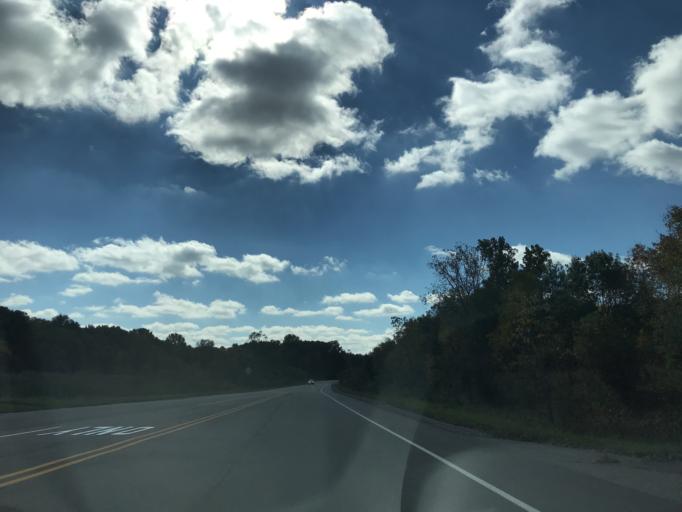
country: US
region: Michigan
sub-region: Washtenaw County
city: Ann Arbor
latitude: 42.3071
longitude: -83.6771
